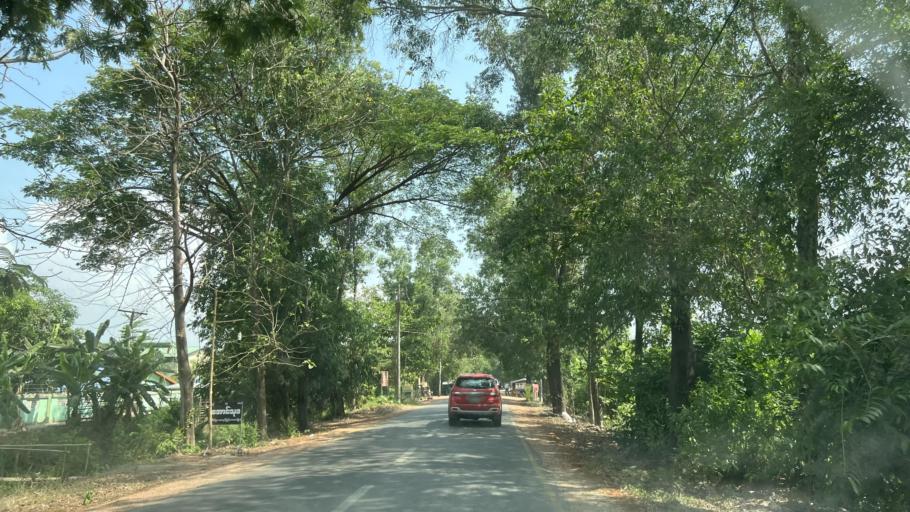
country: MM
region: Yangon
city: Twante
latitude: 16.9305
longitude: 95.9700
